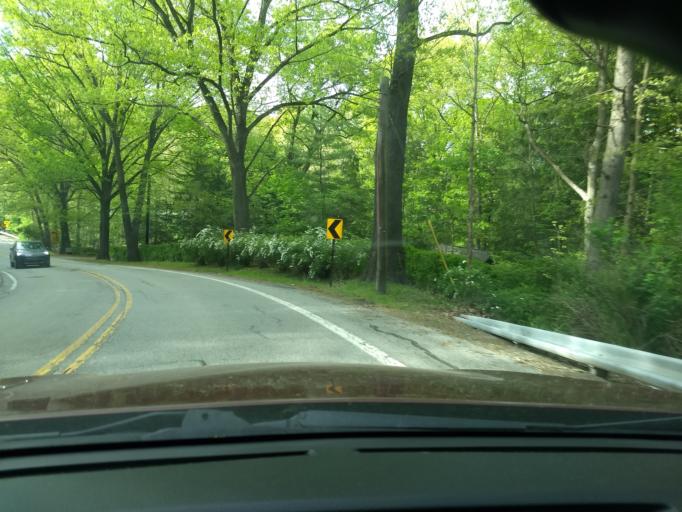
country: US
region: Pennsylvania
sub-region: Allegheny County
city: Russellton
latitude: 40.5857
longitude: -79.8822
